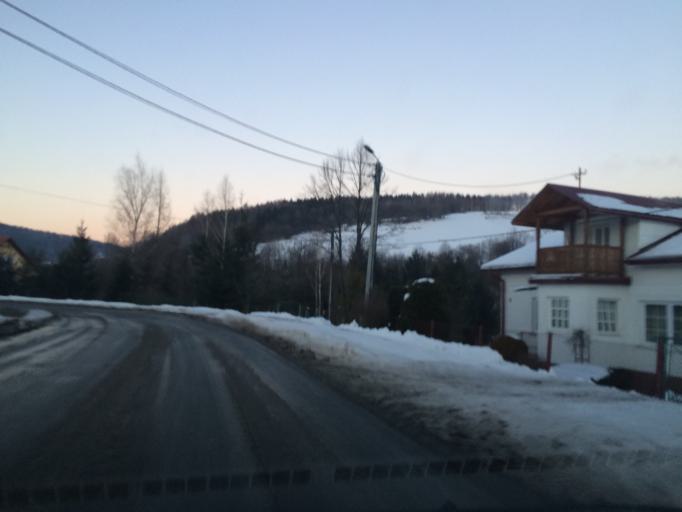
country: PL
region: Subcarpathian Voivodeship
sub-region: Powiat bieszczadzki
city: Ustrzyki Dolne
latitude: 49.4205
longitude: 22.5759
